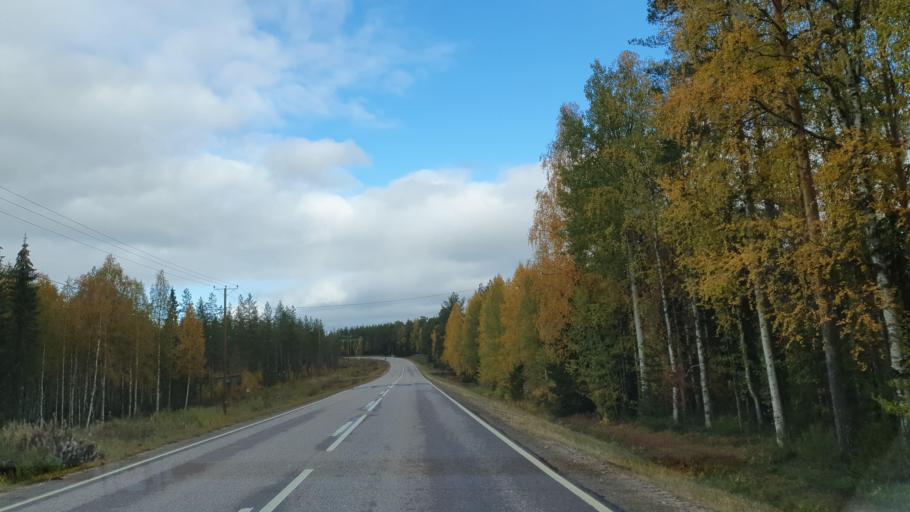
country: FI
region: Lapland
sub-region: Rovaniemi
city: Rovaniemi
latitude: 66.8484
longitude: 25.4394
